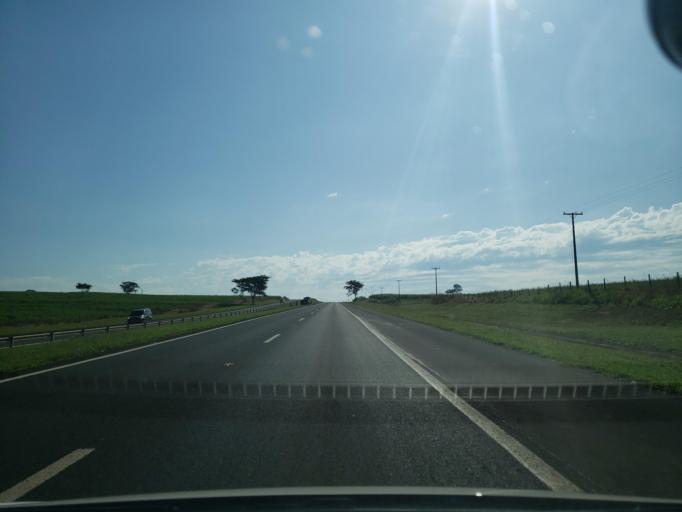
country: BR
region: Sao Paulo
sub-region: Promissao
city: Promissao
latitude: -21.5266
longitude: -49.9906
